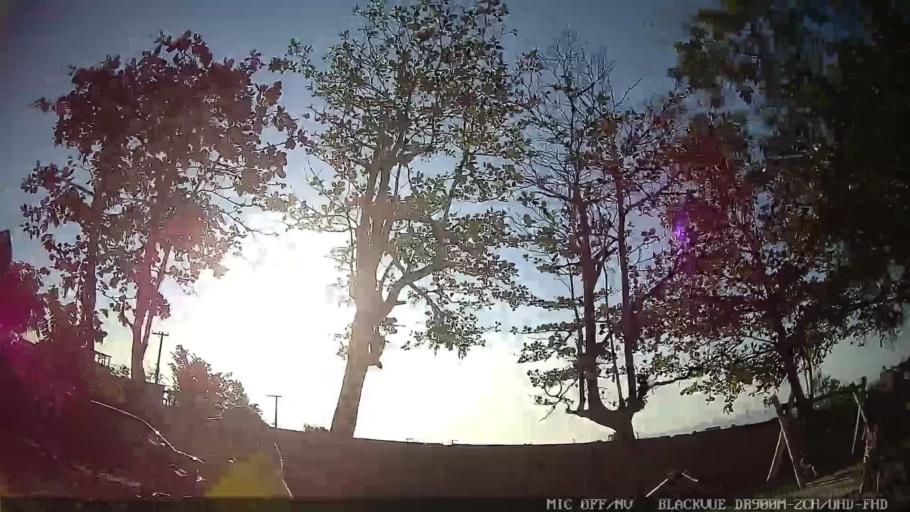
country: BR
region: Sao Paulo
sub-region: Guaruja
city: Guaruja
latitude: -23.9720
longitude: -46.2497
